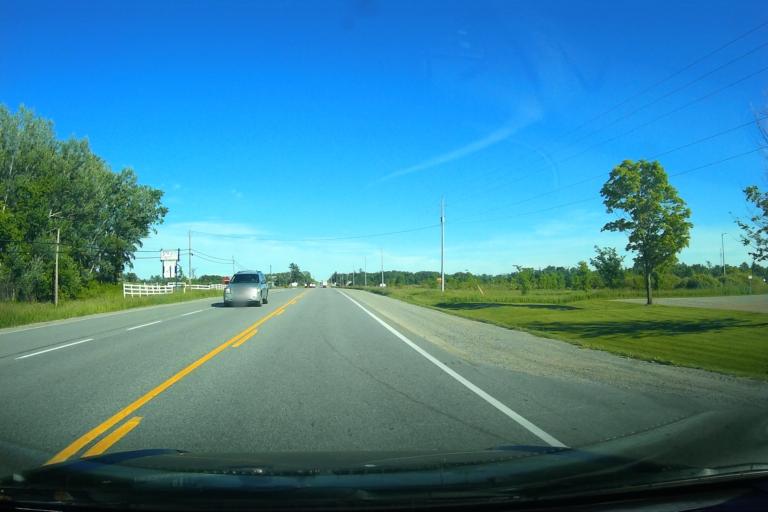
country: CA
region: Quebec
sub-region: Outaouais
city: Fort-Coulonge
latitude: 45.6379
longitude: -76.8954
